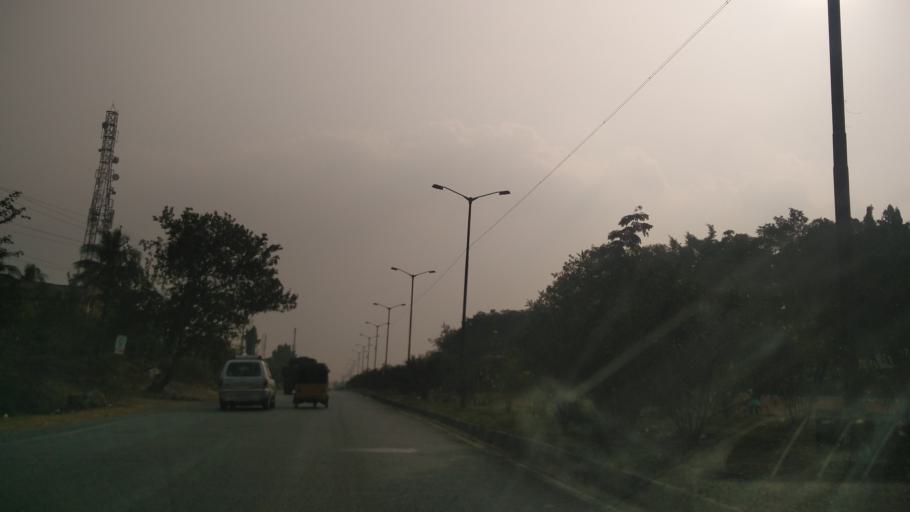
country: IN
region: Andhra Pradesh
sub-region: East Godavari
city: Rajahmundry
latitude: 16.9631
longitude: 81.7955
